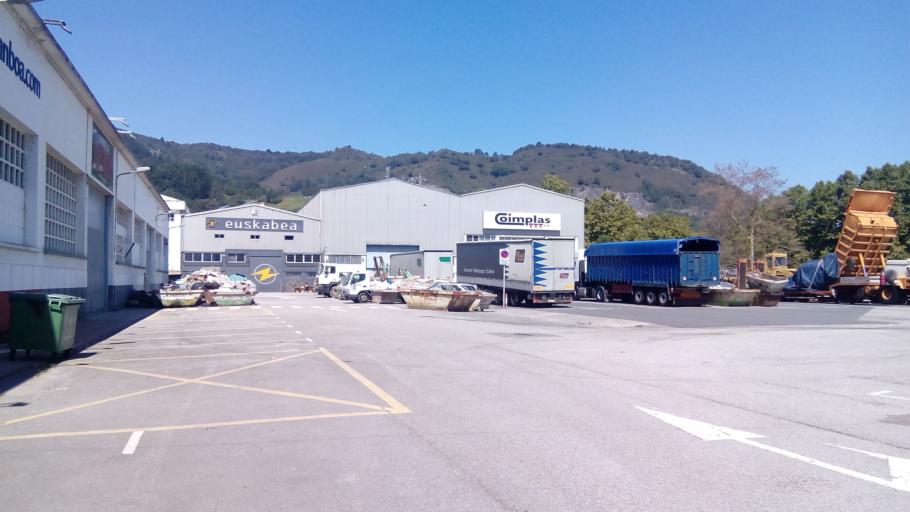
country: ES
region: Basque Country
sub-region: Provincia de Guipuzcoa
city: Andoain
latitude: 43.2193
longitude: -2.0250
